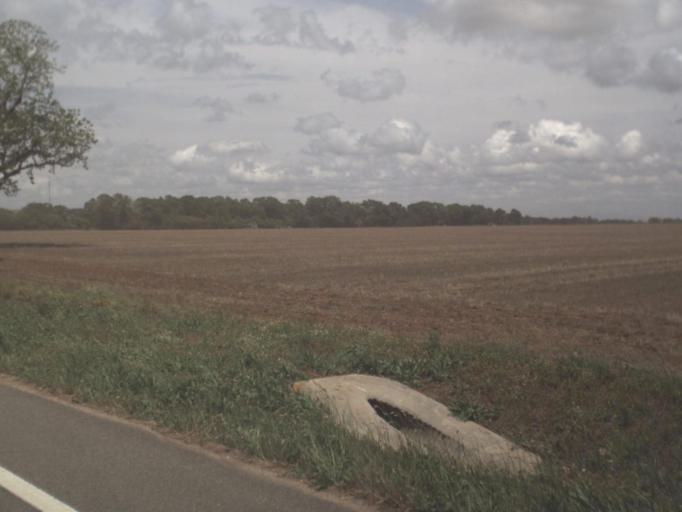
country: US
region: Florida
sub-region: Escambia County
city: Century
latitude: 30.9414
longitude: -87.1559
